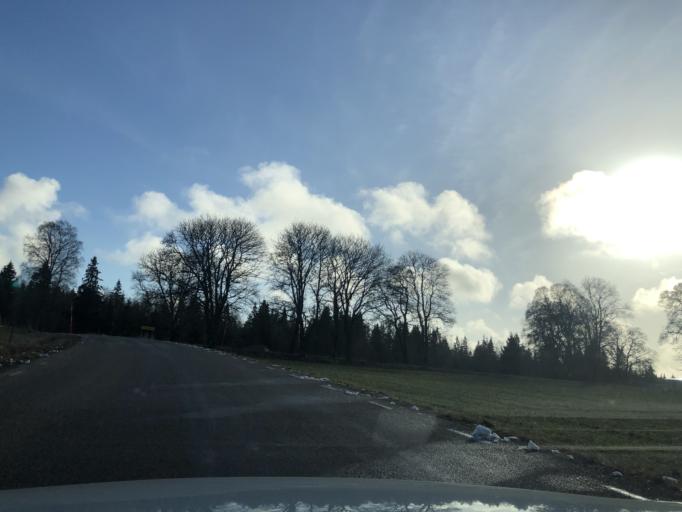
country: SE
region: Vaestra Goetaland
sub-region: Ulricehamns Kommun
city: Ulricehamn
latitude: 57.8038
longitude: 13.5493
